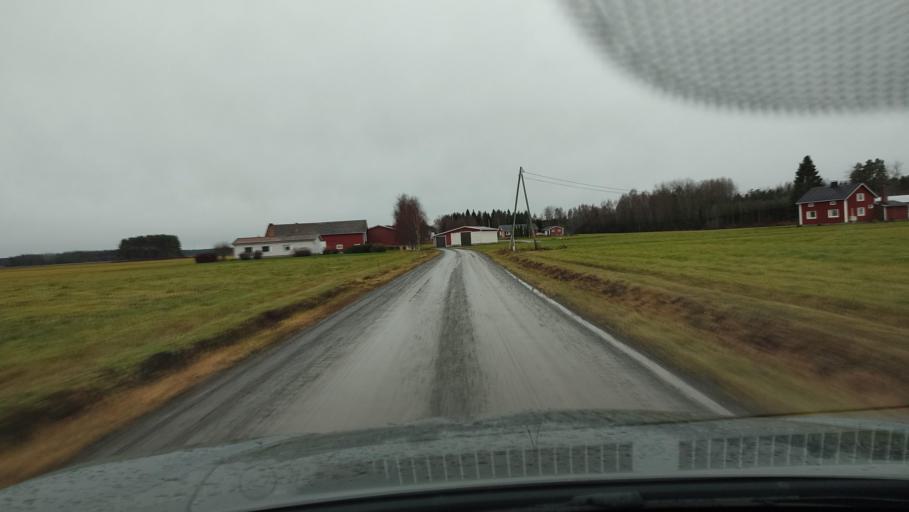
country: FI
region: Southern Ostrobothnia
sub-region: Suupohja
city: Karijoki
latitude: 62.2400
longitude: 21.5513
